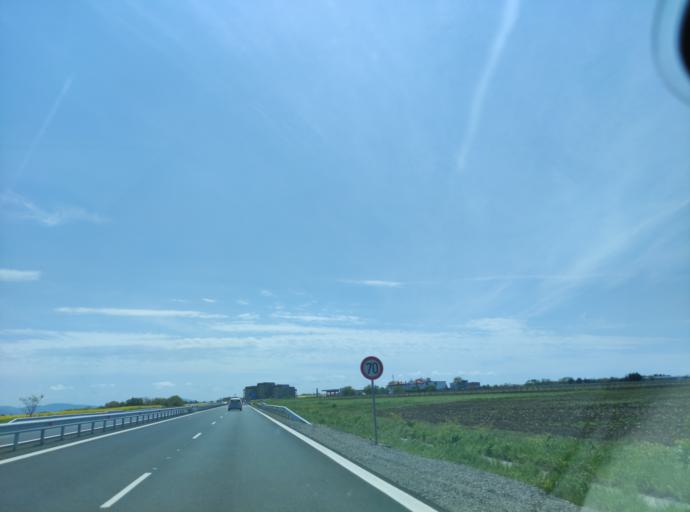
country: BG
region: Burgas
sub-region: Obshtina Pomorie
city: Pomorie
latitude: 42.5651
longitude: 27.5717
